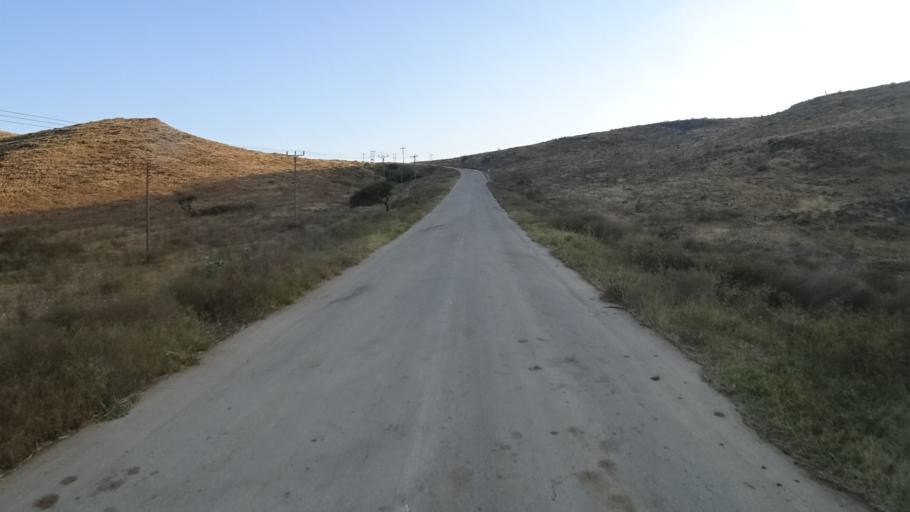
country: OM
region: Zufar
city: Salalah
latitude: 17.1518
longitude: 54.6180
